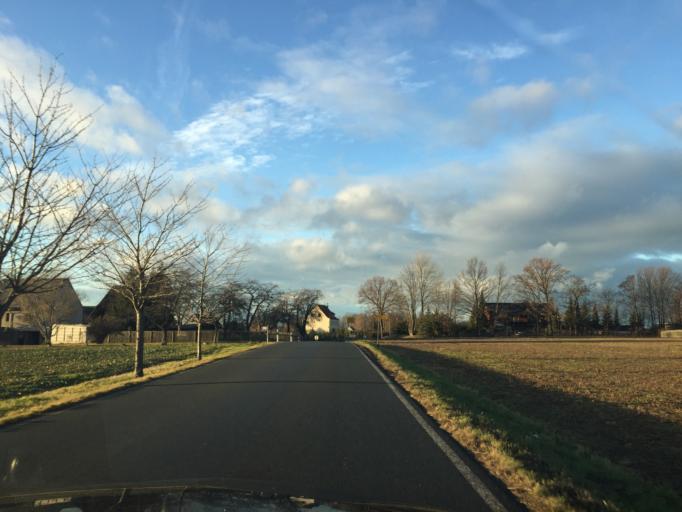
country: DE
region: Thuringia
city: Vollmershain
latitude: 50.8754
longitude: 12.3129
